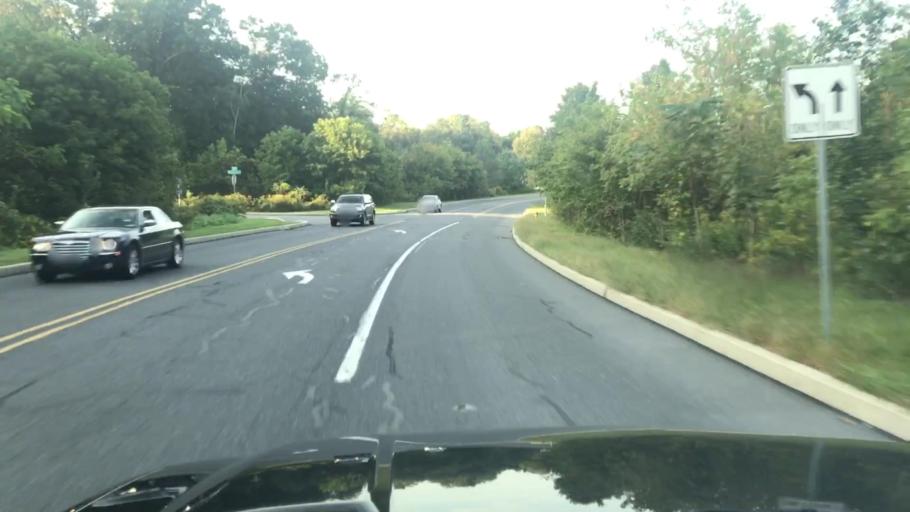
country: US
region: Pennsylvania
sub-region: Cumberland County
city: Enola
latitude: 40.2798
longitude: -76.9788
